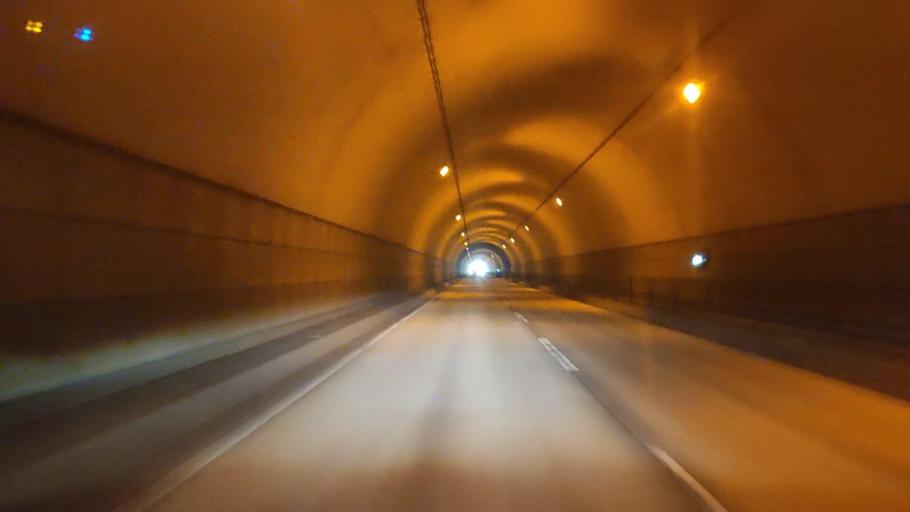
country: JP
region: Miyazaki
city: Nobeoka
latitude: 32.6725
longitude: 131.7700
